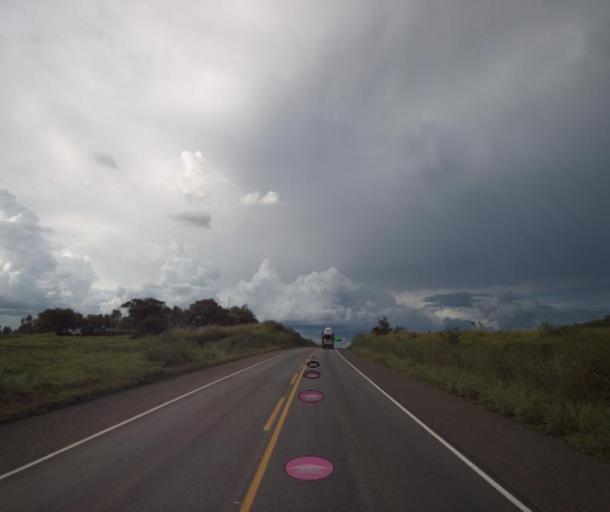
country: BR
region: Goias
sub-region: Ceres
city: Ceres
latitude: -15.2275
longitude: -49.5544
